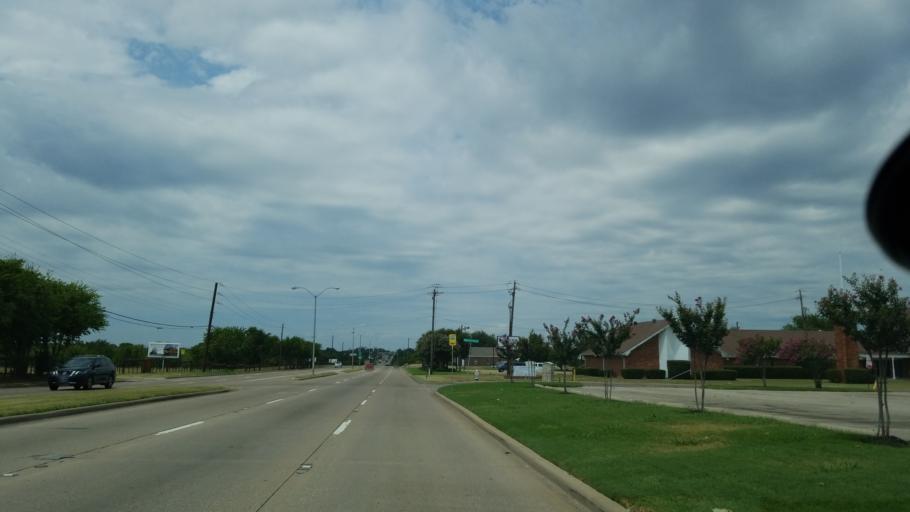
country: US
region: Texas
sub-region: Dallas County
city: Duncanville
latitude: 32.6578
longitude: -96.8570
